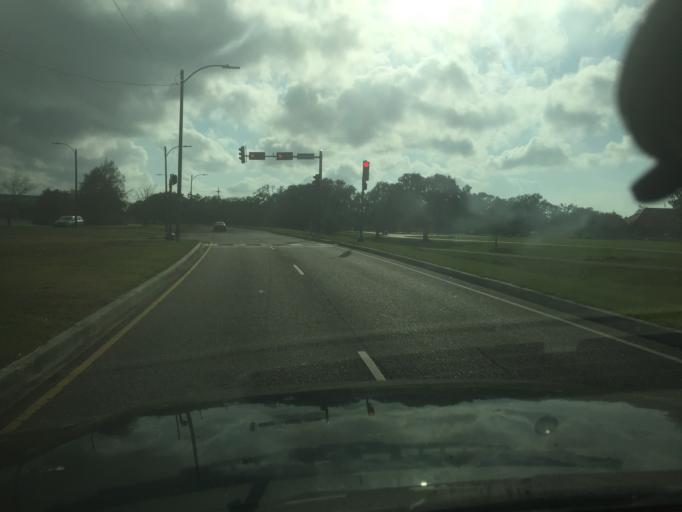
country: US
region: Louisiana
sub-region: Orleans Parish
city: New Orleans
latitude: 29.9897
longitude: -90.0879
